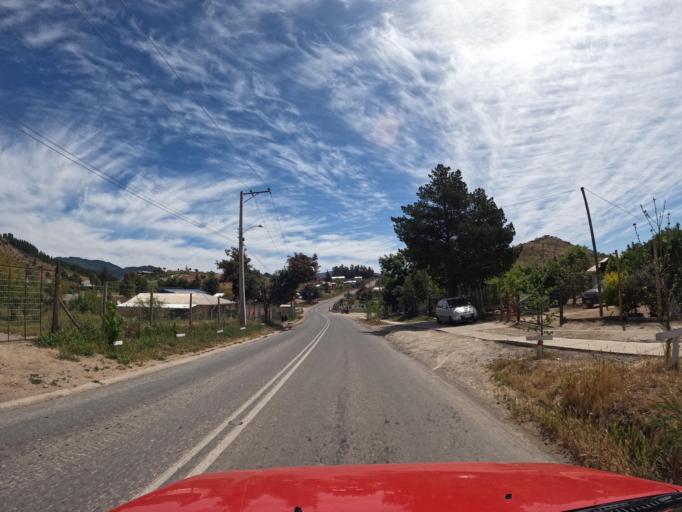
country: CL
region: Maule
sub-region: Provincia de Talca
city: Talca
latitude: -35.1199
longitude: -71.6810
